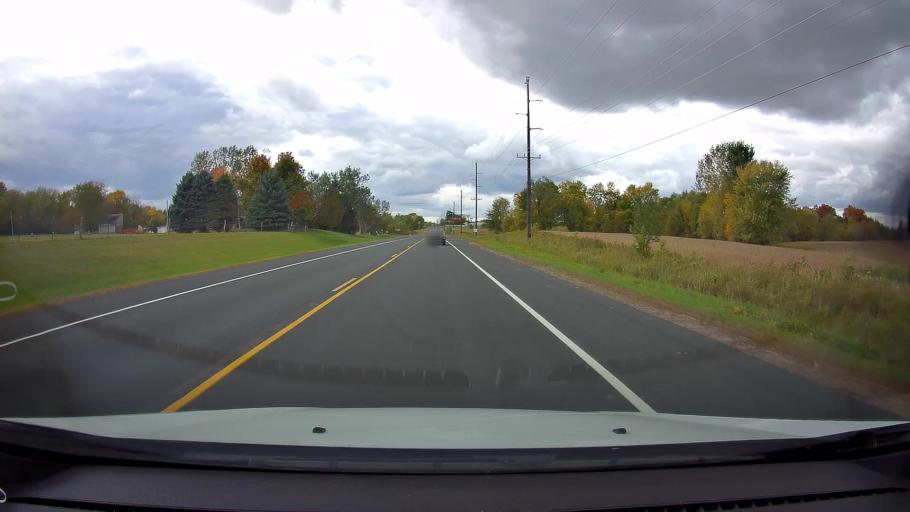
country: US
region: Minnesota
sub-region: Chisago County
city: Shafer
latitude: 45.3972
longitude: -92.7721
